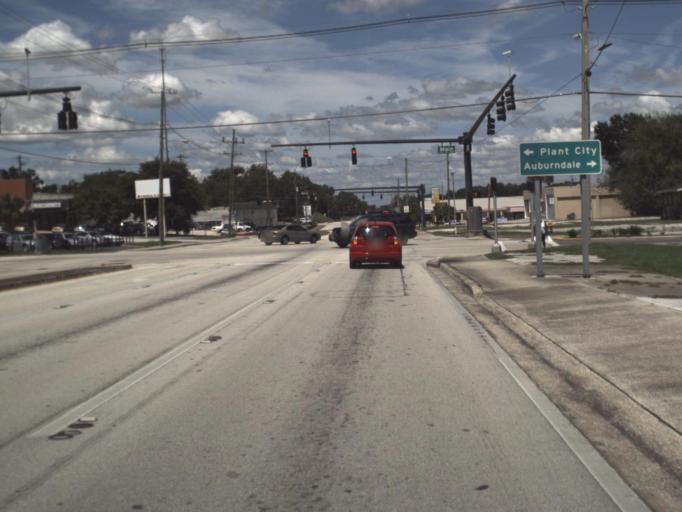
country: US
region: Florida
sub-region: Polk County
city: Lakeland
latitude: 28.0437
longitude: -81.9407
